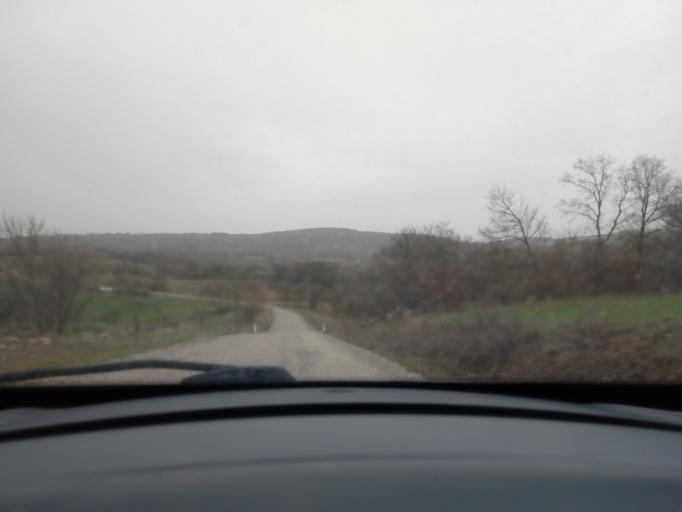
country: TR
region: Balikesir
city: Susurluk
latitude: 39.9211
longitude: 28.0763
